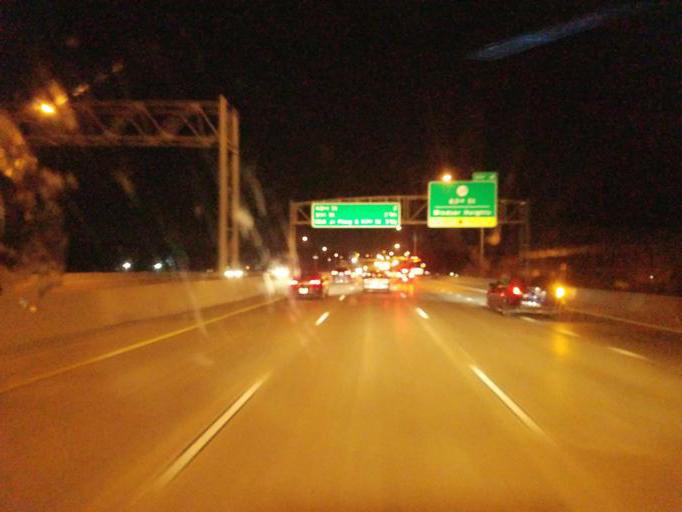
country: US
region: Iowa
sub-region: Polk County
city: Windsor Heights
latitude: 41.5933
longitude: -93.7147
